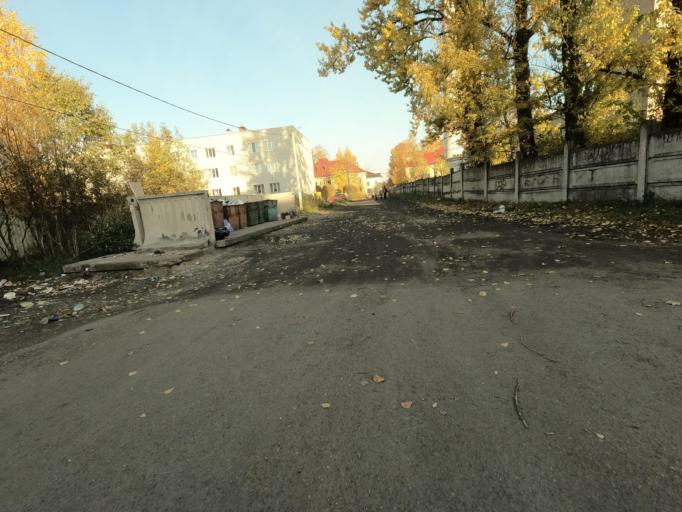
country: RU
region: Leningrad
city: Mga
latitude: 59.7583
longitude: 31.0593
